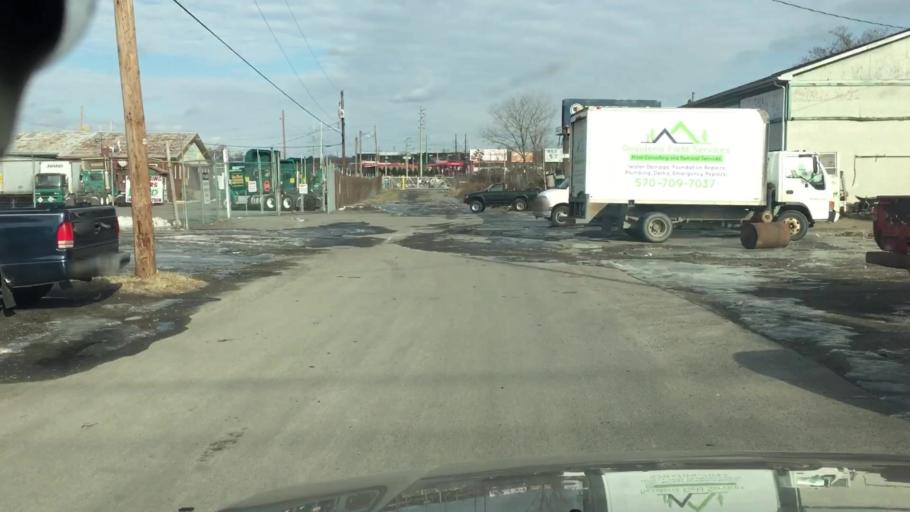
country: US
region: Pennsylvania
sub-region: Luzerne County
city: Georgetown
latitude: 41.2318
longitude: -75.8714
